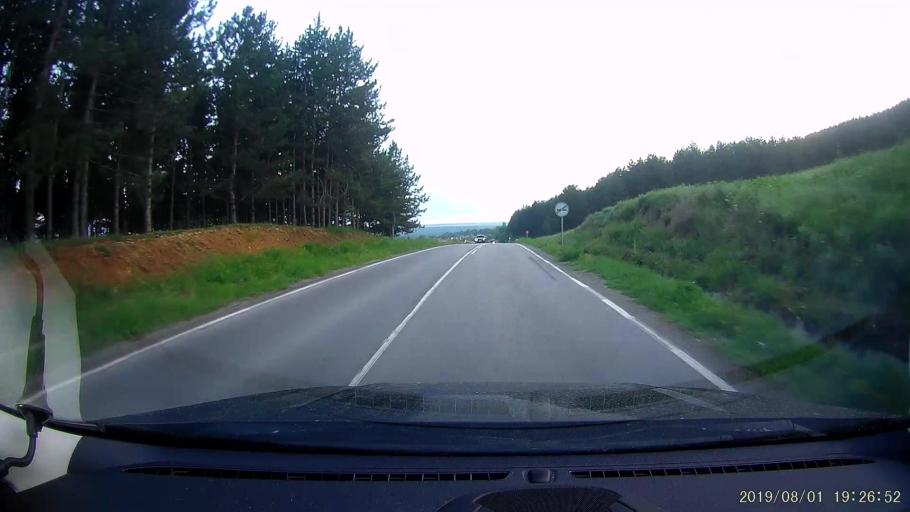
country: BG
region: Burgas
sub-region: Obshtina Sungurlare
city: Sungurlare
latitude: 42.8538
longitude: 26.9364
